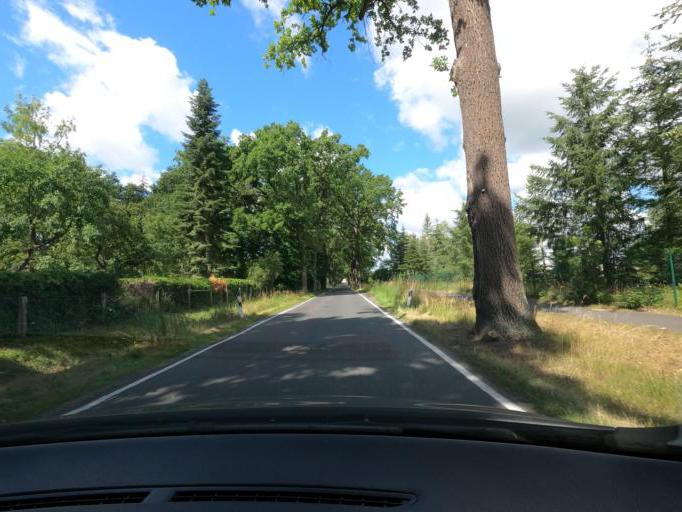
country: DE
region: Brandenburg
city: Kremmen
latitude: 52.7286
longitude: 12.9655
